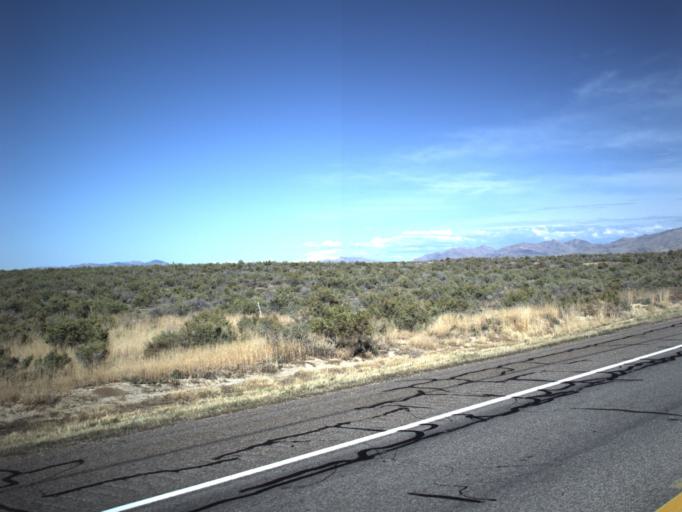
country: US
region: Utah
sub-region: Millard County
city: Delta
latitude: 39.3533
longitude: -112.5014
